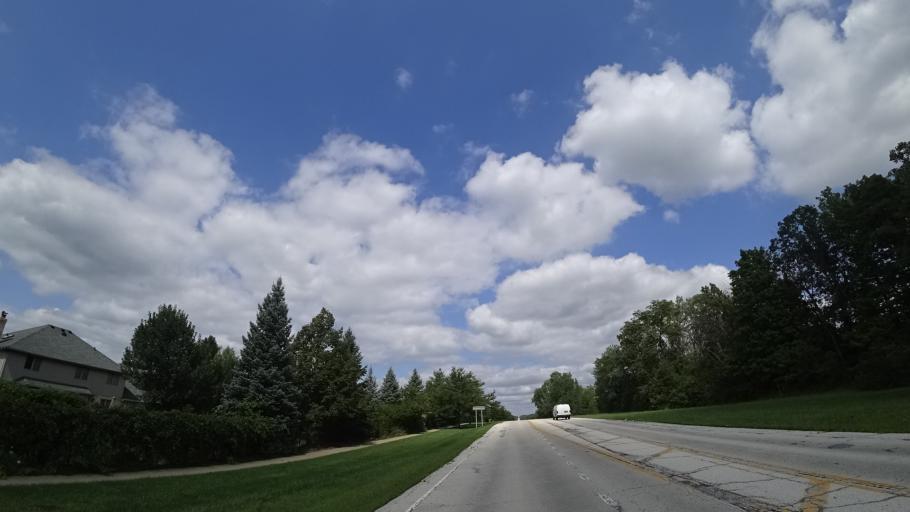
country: US
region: Illinois
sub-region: Cook County
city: Orland Hills
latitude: 41.5654
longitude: -87.8711
